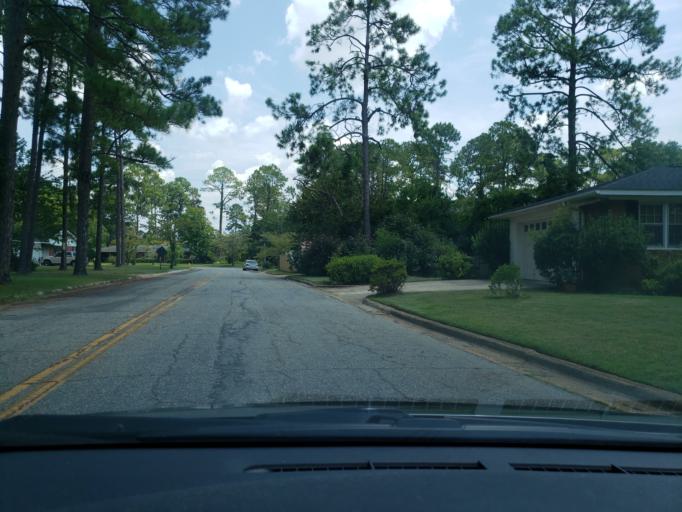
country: US
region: Georgia
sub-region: Dougherty County
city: Albany
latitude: 31.5998
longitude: -84.2057
